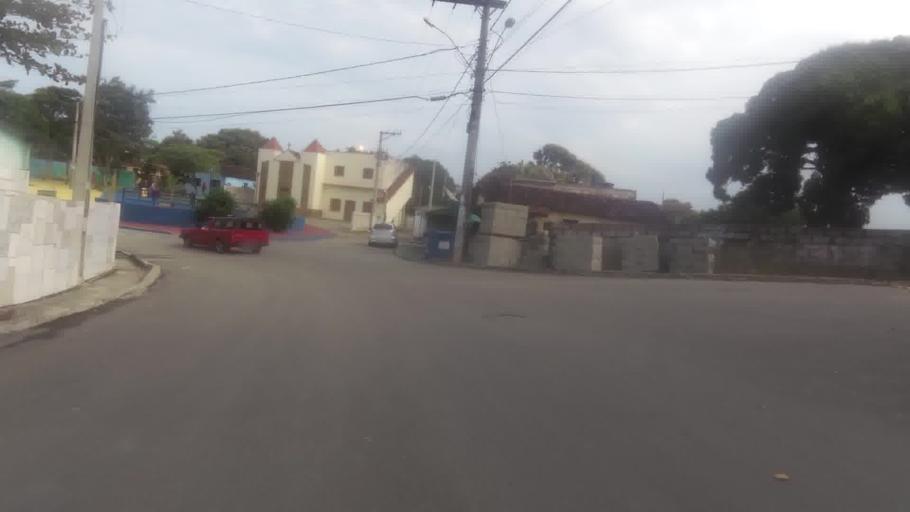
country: BR
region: Espirito Santo
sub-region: Guarapari
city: Guarapari
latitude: -20.7656
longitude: -40.5760
